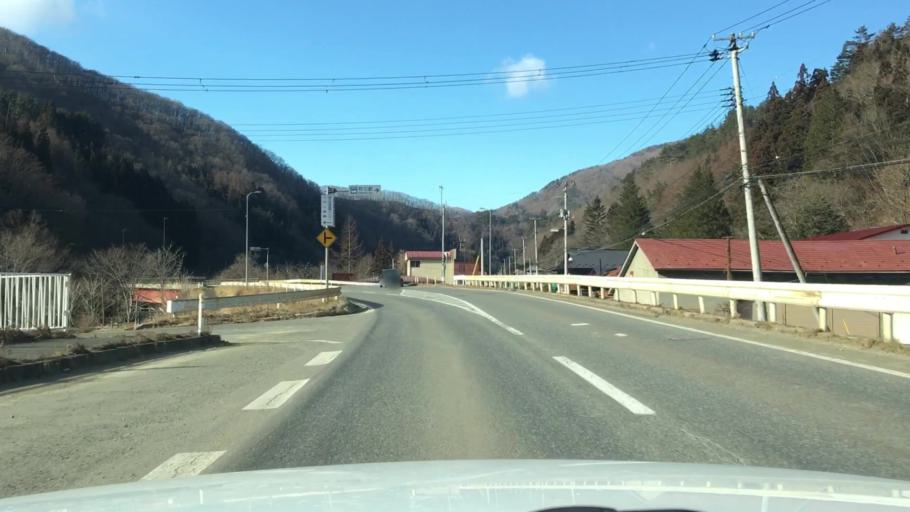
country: JP
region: Iwate
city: Tono
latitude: 39.6145
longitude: 141.6278
